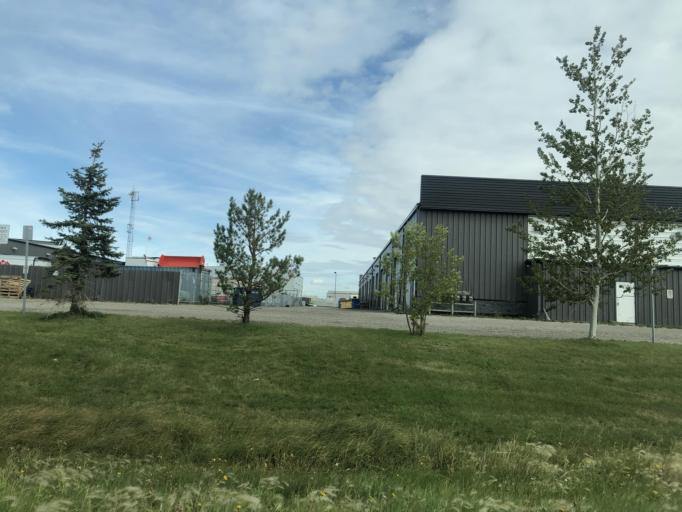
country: CA
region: Alberta
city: Chestermere
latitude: 50.9615
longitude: -113.9085
